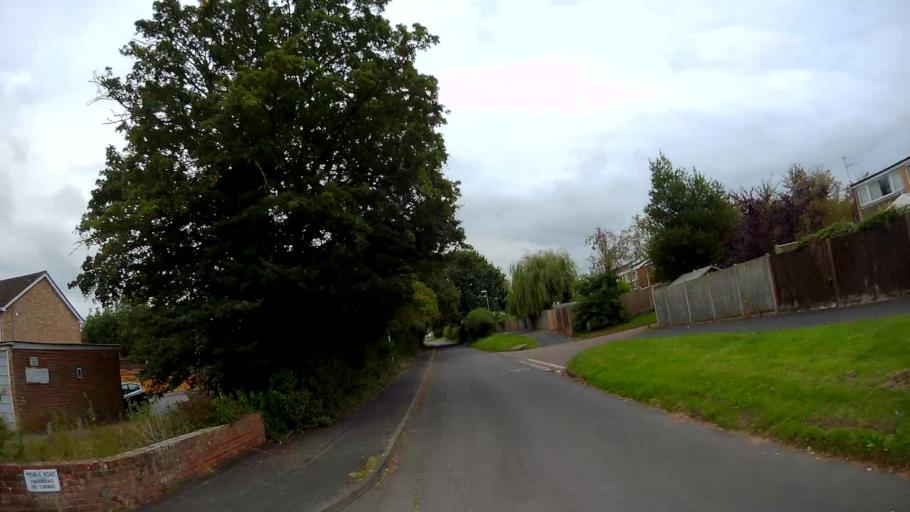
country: GB
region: England
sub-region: Hampshire
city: Basingstoke
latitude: 51.2531
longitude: -1.0990
